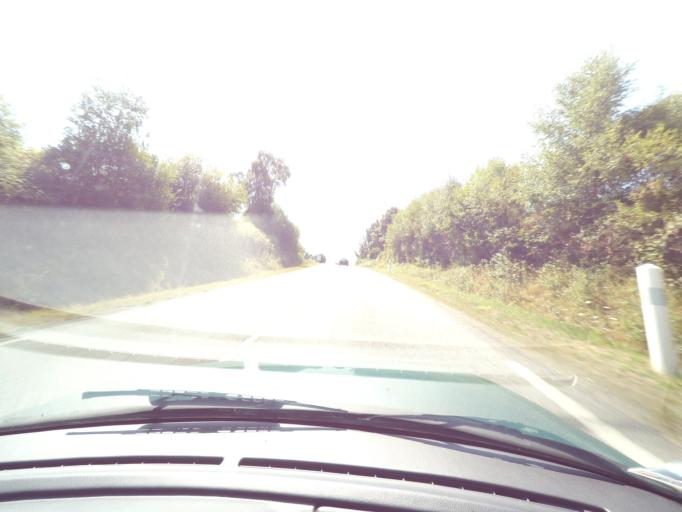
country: FR
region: Limousin
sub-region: Departement de la Haute-Vienne
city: Chaptelat
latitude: 45.9106
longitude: 1.2193
